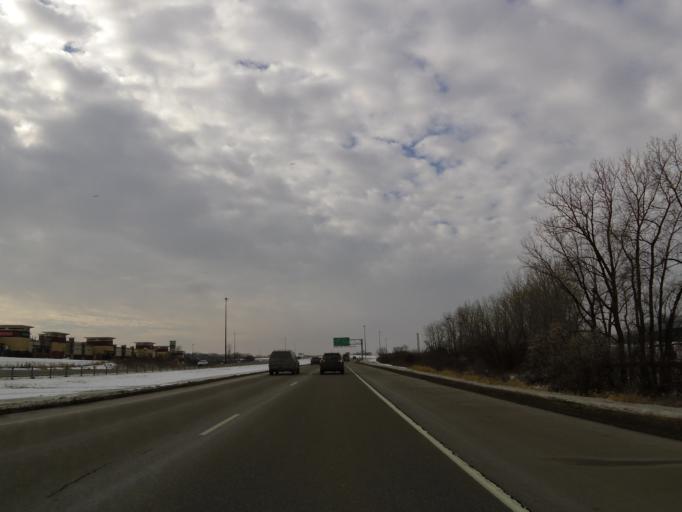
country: US
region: Minnesota
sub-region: Dakota County
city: Eagan
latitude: 44.8178
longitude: -93.2127
